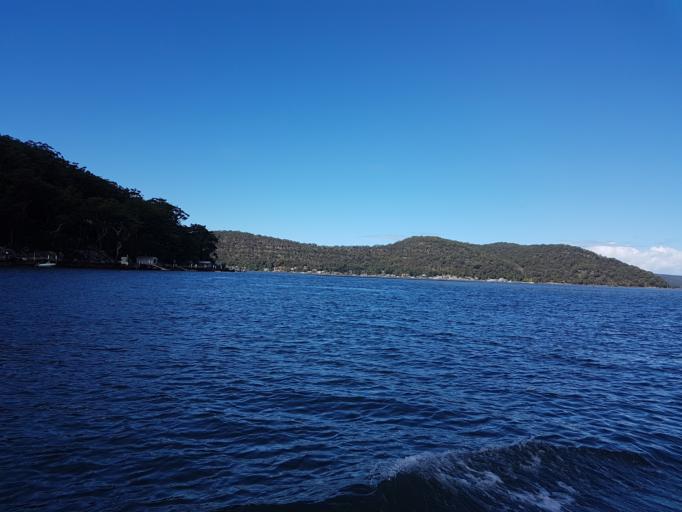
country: AU
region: New South Wales
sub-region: Gosford Shire
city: Umina
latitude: -33.5419
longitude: 151.2334
